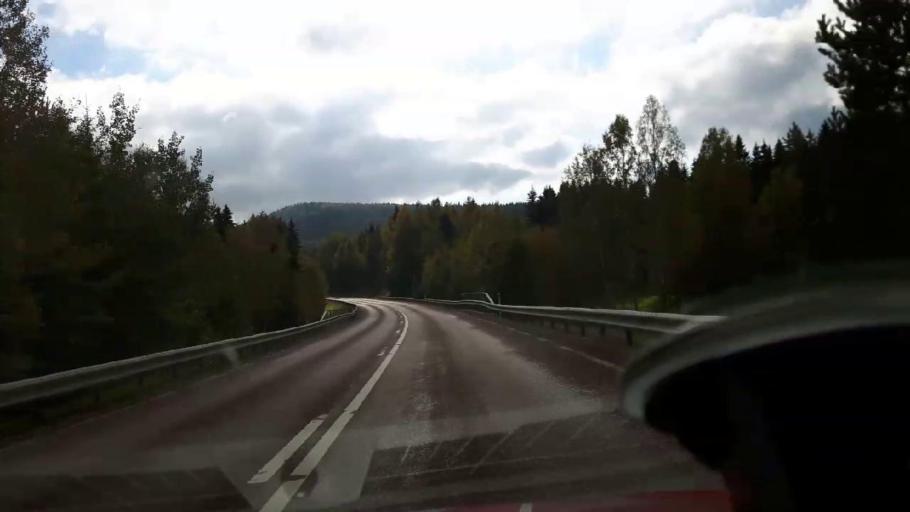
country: SE
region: Gaevleborg
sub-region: Bollnas Kommun
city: Arbra
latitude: 61.5774
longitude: 16.3166
